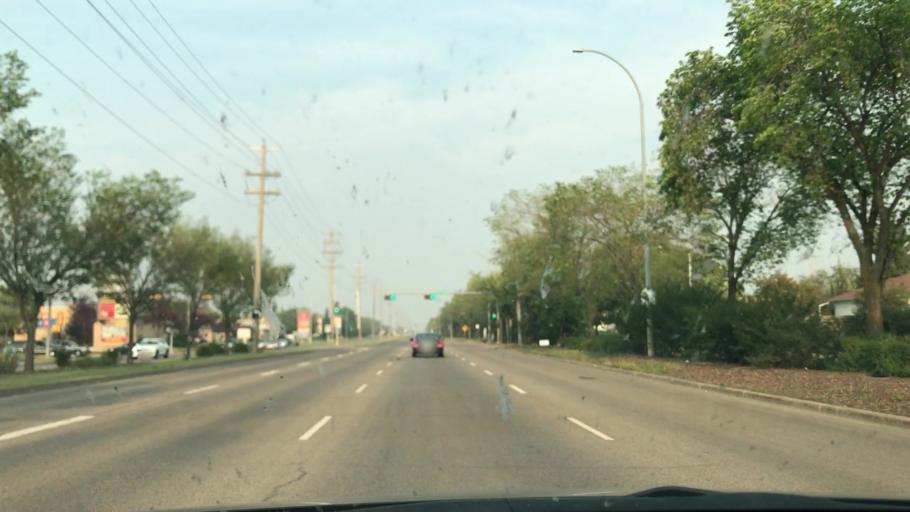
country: CA
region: Alberta
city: Edmonton
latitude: 53.5993
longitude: -113.5363
